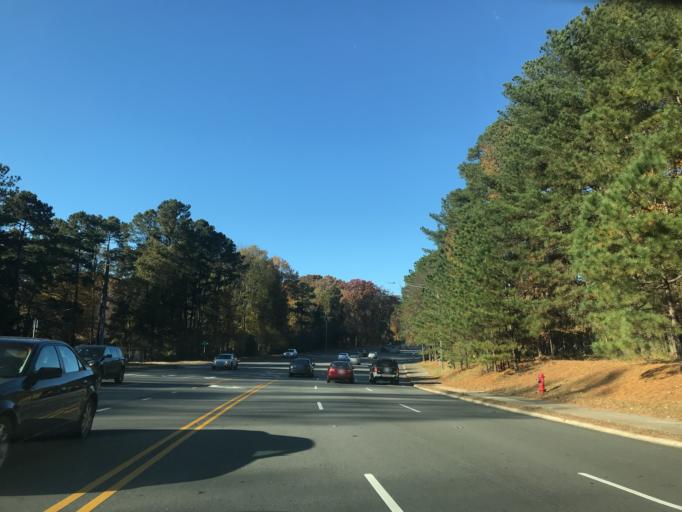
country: US
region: North Carolina
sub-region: Wake County
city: West Raleigh
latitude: 35.8443
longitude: -78.6142
